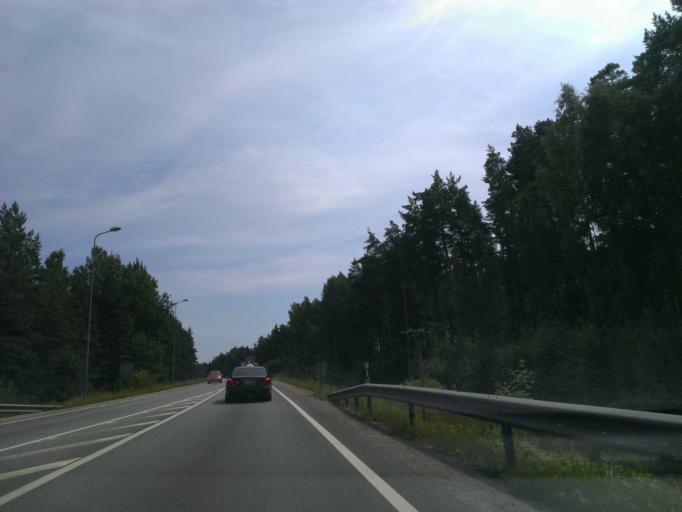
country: LV
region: Riga
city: Bergi
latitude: 56.9721
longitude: 24.3439
